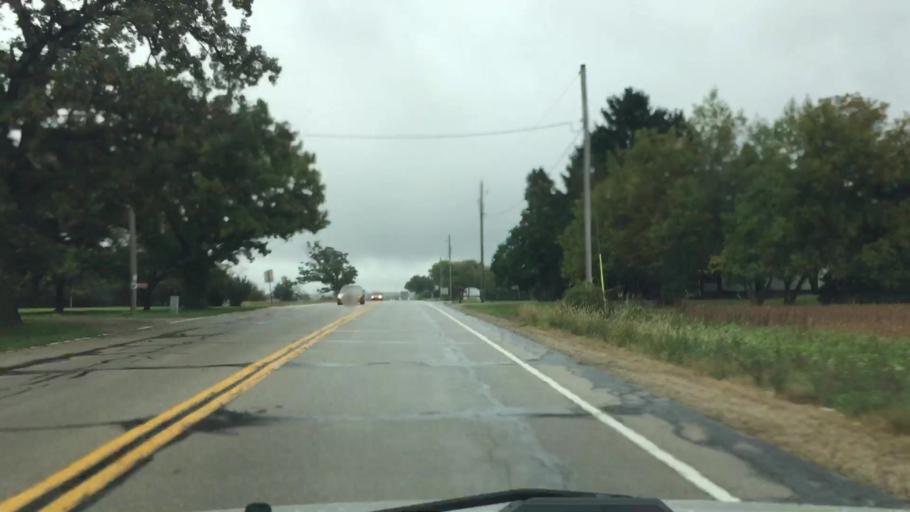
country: US
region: Wisconsin
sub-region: Walworth County
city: Whitewater
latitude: 42.8267
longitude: -88.7059
